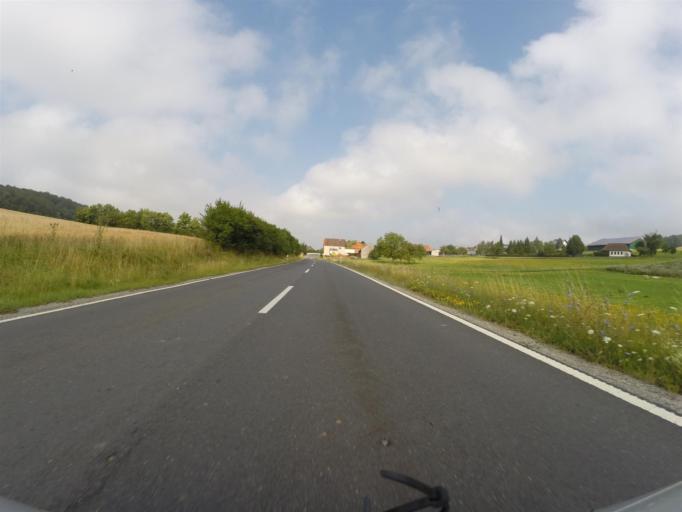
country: DE
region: Hesse
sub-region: Regierungsbezirk Kassel
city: Weissenborn
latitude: 51.0858
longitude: 10.1337
